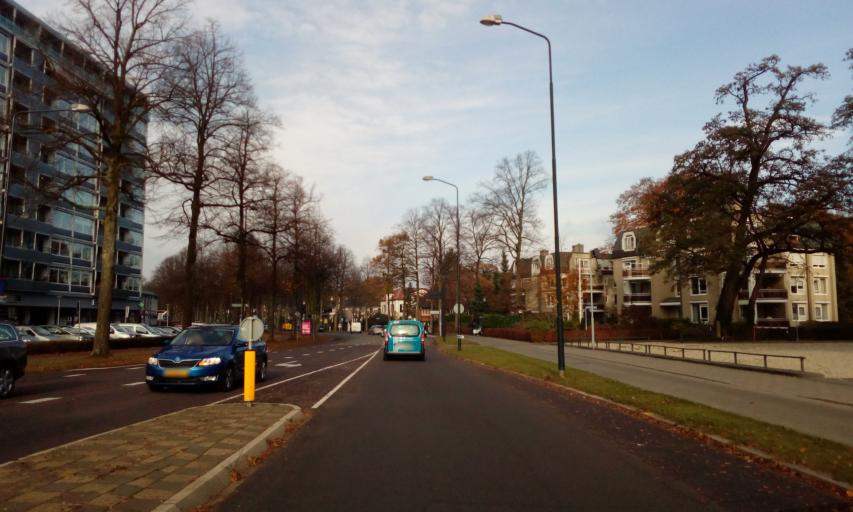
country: NL
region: Gelderland
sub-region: Gemeente Apeldoorn
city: Apeldoorn
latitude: 52.2203
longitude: 5.9547
